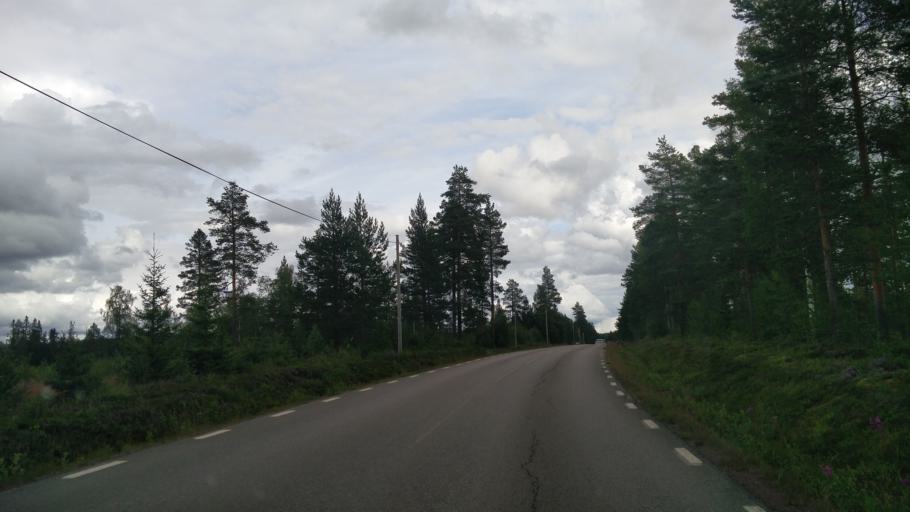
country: NO
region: Hedmark
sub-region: Trysil
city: Innbygda
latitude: 61.1645
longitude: 12.8249
